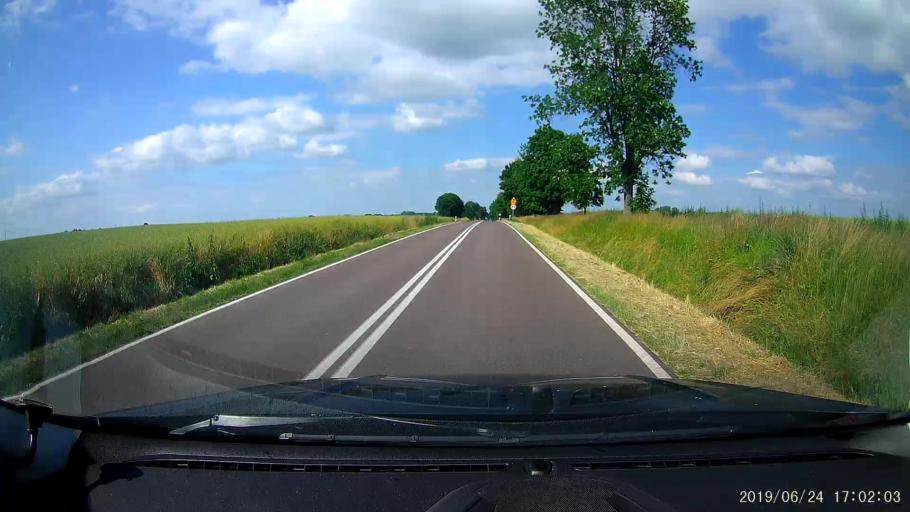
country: PL
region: Lublin Voivodeship
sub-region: Powiat tomaszowski
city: Telatyn
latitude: 50.5469
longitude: 23.9283
